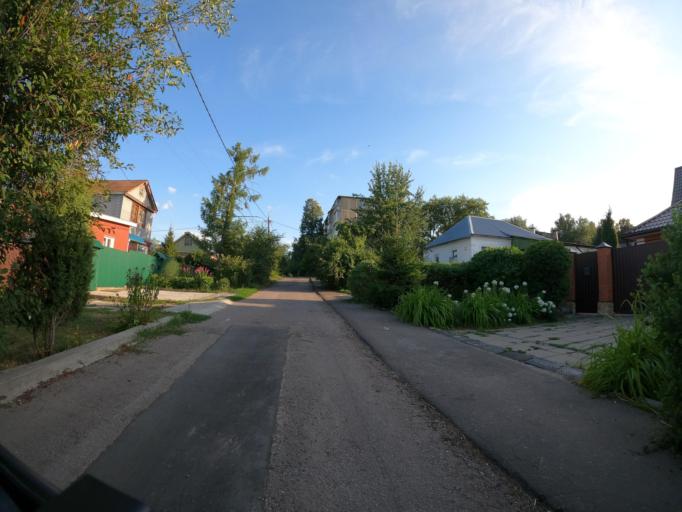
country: RU
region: Moskovskaya
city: Raduzhnyy
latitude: 55.1101
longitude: 38.7322
